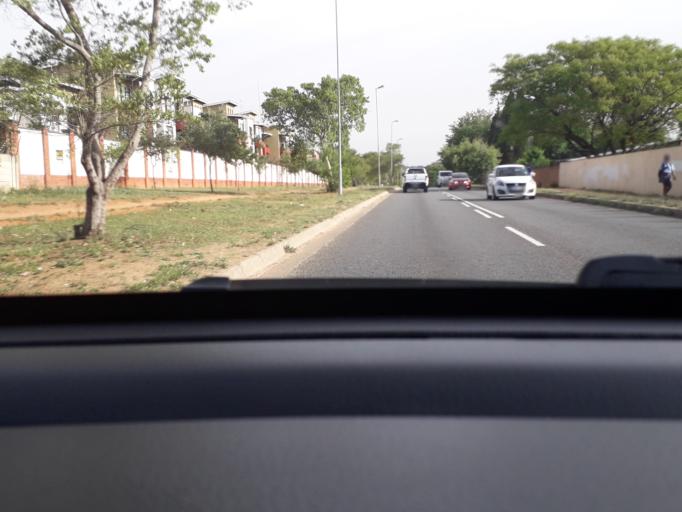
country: ZA
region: Gauteng
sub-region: City of Johannesburg Metropolitan Municipality
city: Diepsloot
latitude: -26.0310
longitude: 27.9920
